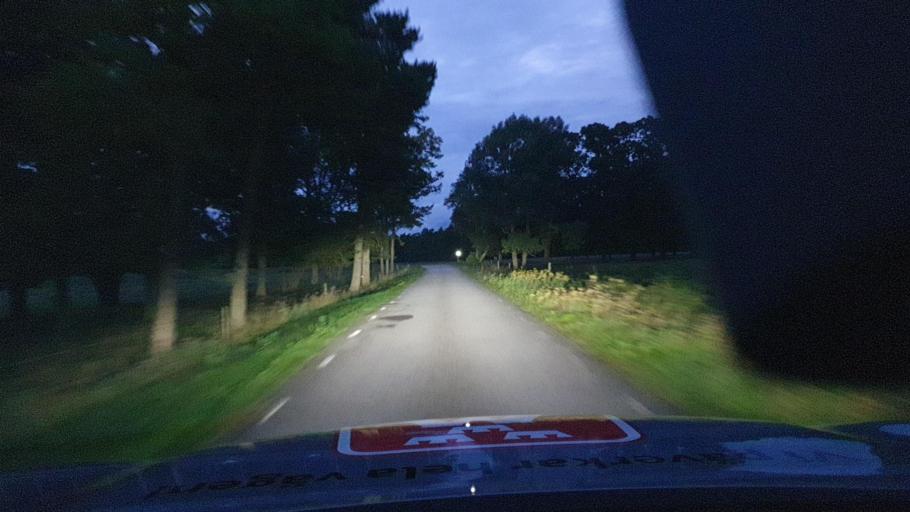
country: SE
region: Gotland
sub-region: Gotland
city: Slite
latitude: 57.7795
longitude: 18.6447
